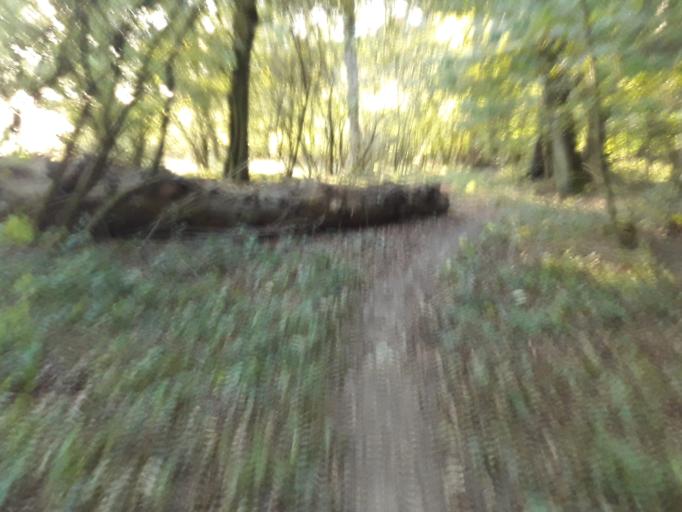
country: DE
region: North Rhine-Westphalia
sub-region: Regierungsbezirk Detmold
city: Schlangen
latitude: 51.7915
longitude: 8.8747
